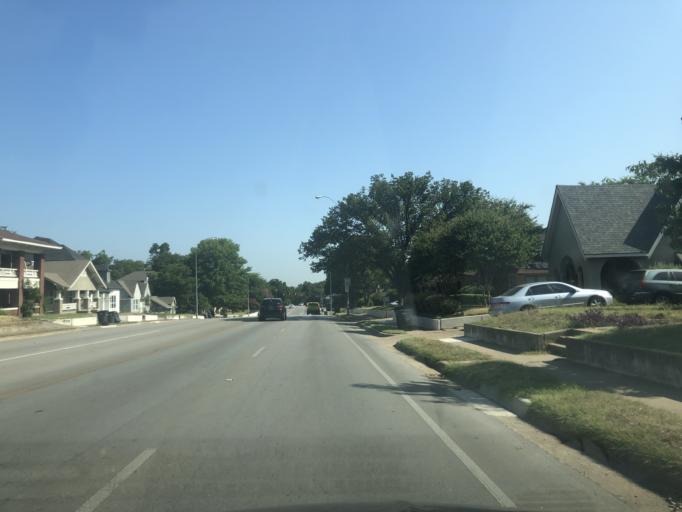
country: US
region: Texas
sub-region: Tarrant County
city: Fort Worth
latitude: 32.7138
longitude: -97.3603
